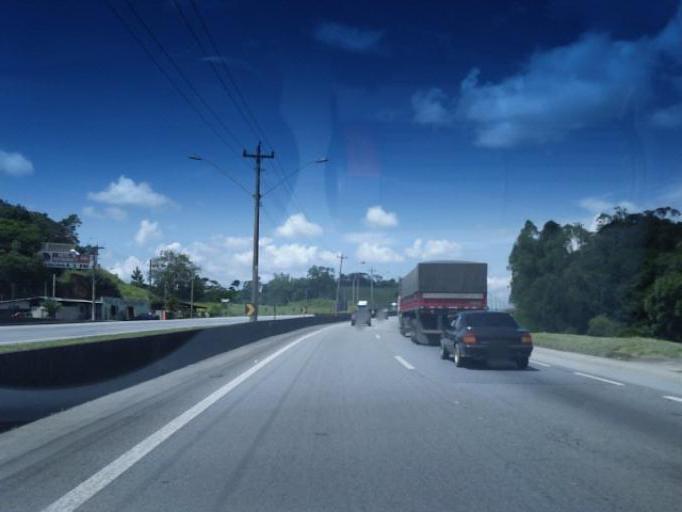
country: BR
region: Sao Paulo
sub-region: Sao Lourenco Da Serra
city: Sao Lourenco da Serra
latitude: -23.8650
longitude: -46.9494
